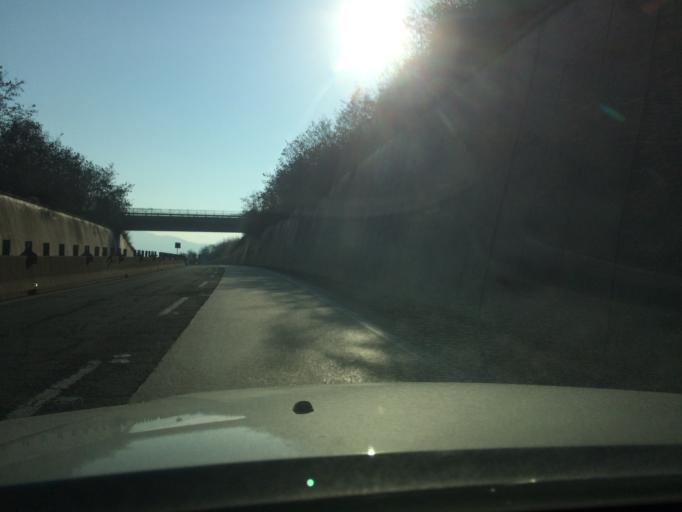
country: IT
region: Umbria
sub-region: Provincia di Perugia
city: Ponterio-Pian di Porto
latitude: 42.8266
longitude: 12.3989
